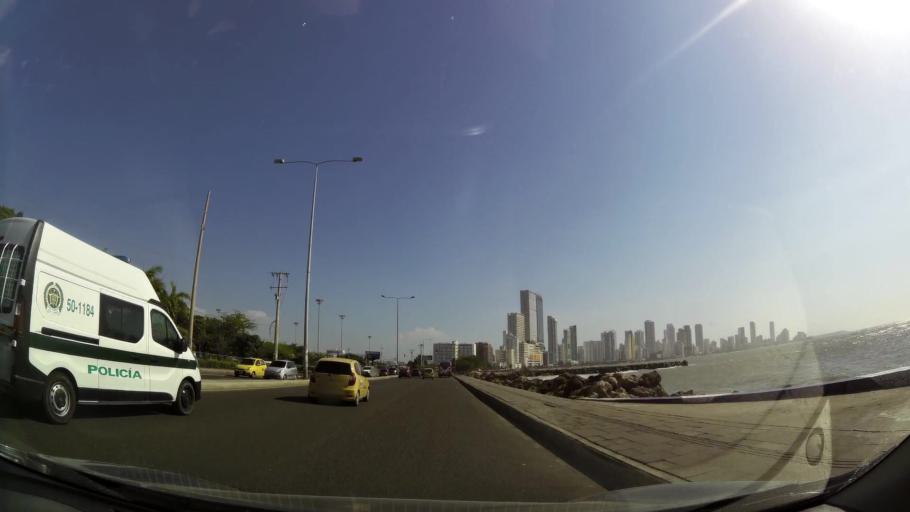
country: CO
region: Bolivar
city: Cartagena
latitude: 10.4202
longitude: -75.5531
